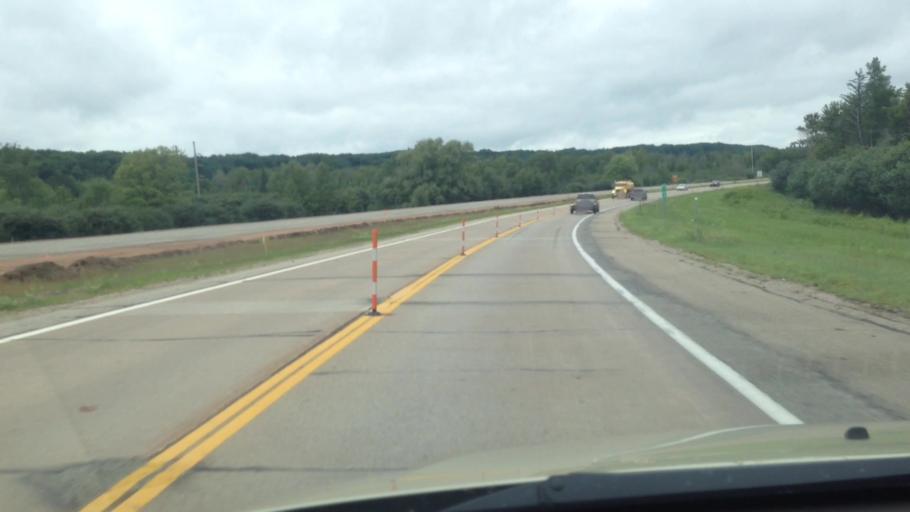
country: US
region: Michigan
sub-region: Delta County
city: Gladstone
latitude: 45.8623
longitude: -87.0266
